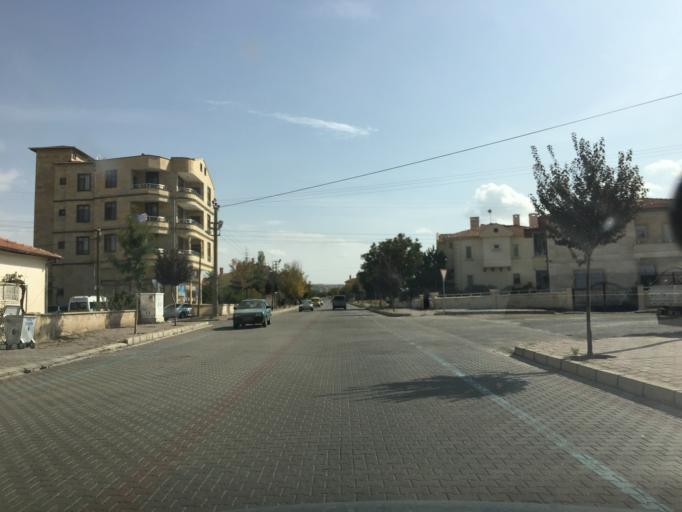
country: TR
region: Nevsehir
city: Avanos
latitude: 38.7074
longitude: 34.8520
